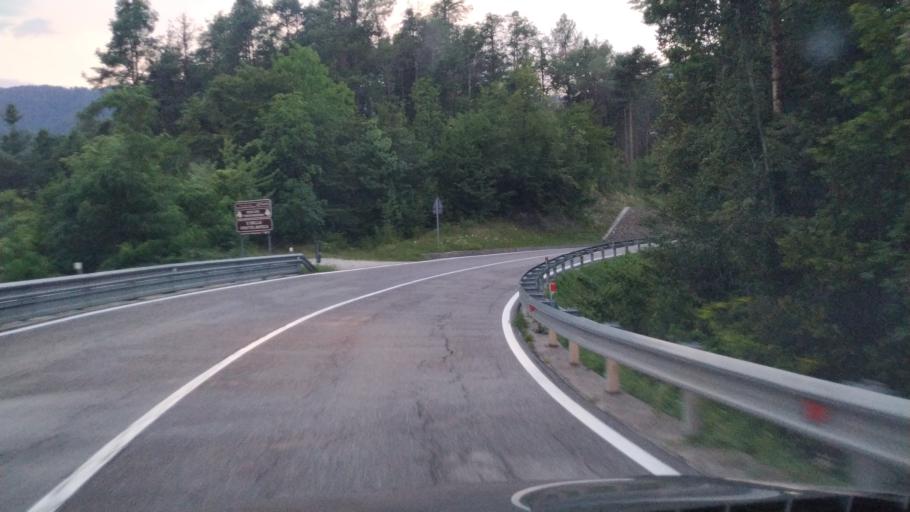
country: IT
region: Trentino-Alto Adige
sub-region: Provincia di Trento
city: Castelfondo
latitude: 46.4432
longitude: 11.1225
